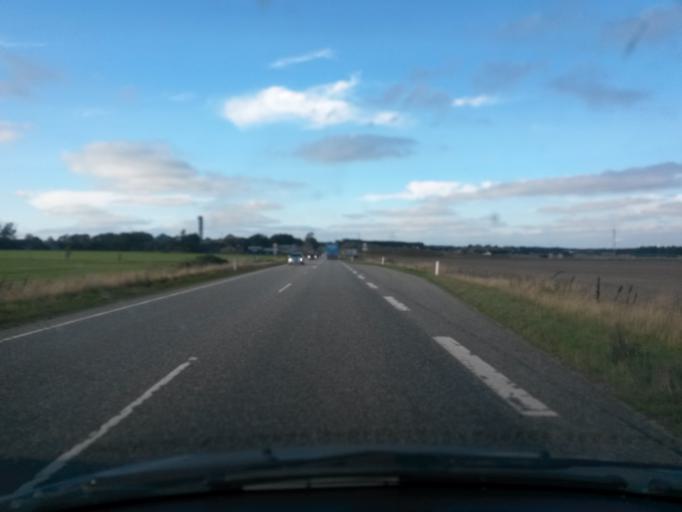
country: DK
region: Central Jutland
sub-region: Holstebro Kommune
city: Holstebro
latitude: 56.3272
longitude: 8.6636
